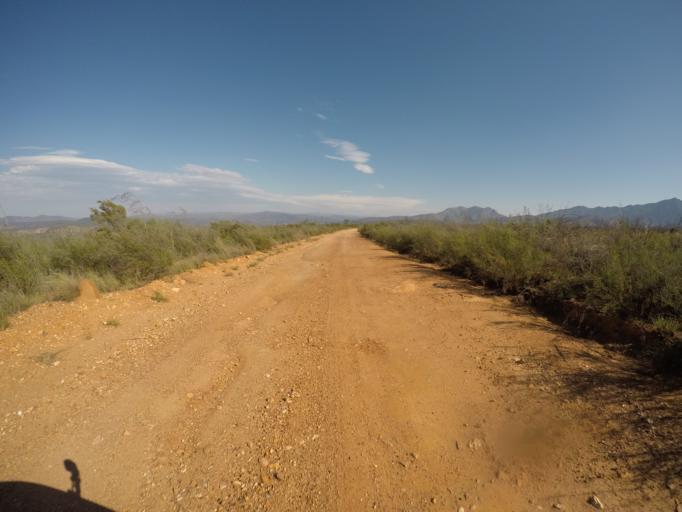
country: ZA
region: Eastern Cape
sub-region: Cacadu District Municipality
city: Kareedouw
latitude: -33.6354
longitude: 24.4665
